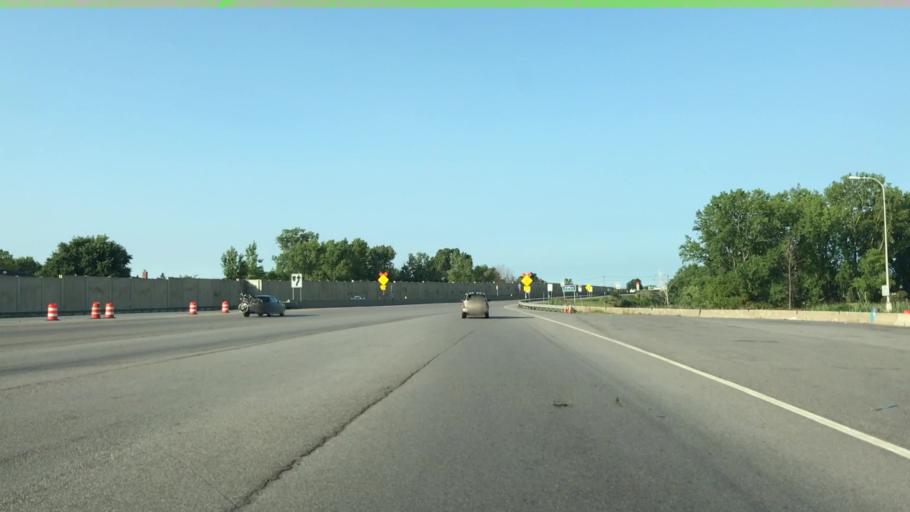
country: US
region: New York
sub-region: Erie County
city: Lackawanna
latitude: 42.8138
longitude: -78.7946
